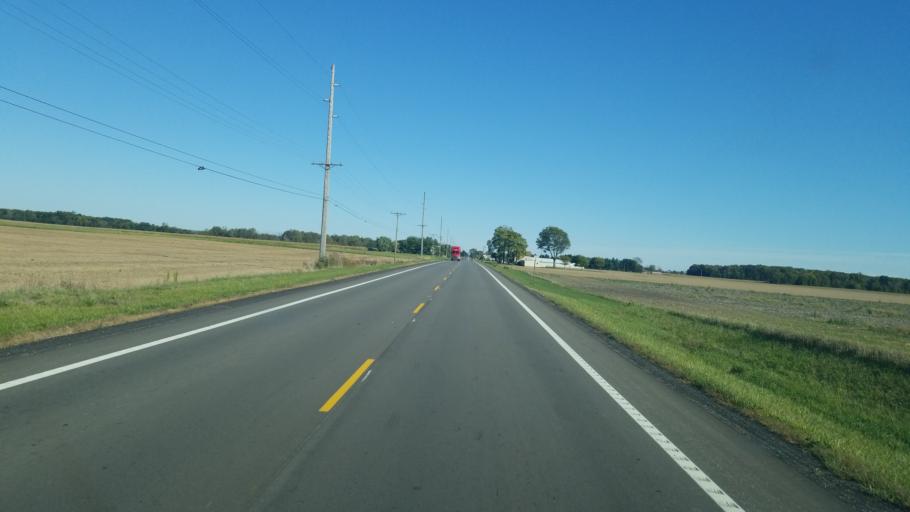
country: US
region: Ohio
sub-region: Wayne County
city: West Salem
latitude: 41.0274
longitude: -82.1555
